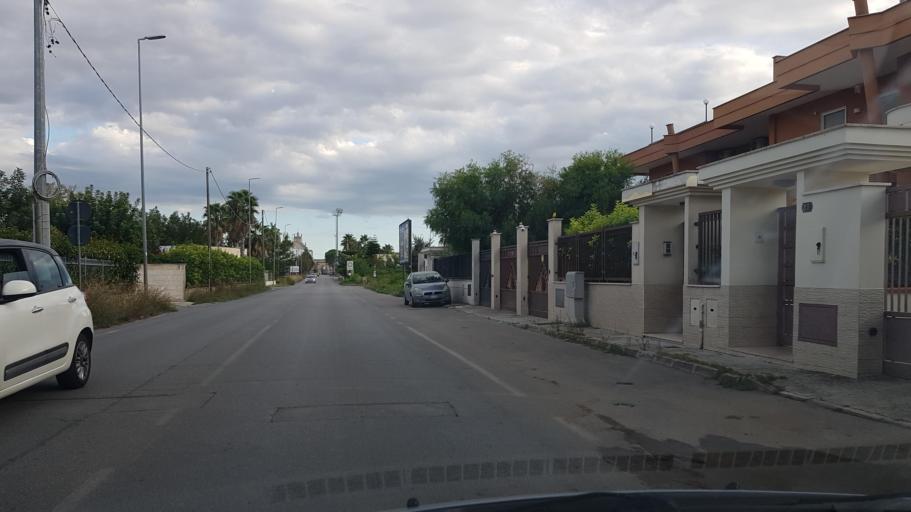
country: IT
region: Apulia
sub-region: Provincia di Brindisi
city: Francavilla Fontana
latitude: 40.5381
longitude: 17.5766
